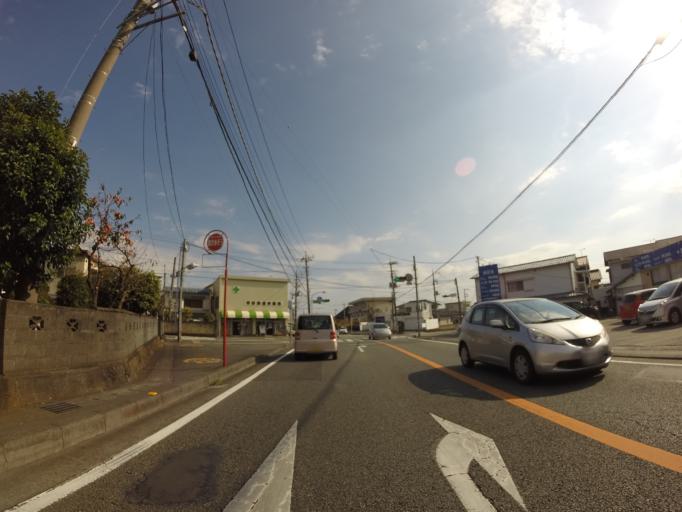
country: JP
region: Shizuoka
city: Fujinomiya
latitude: 35.2169
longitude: 138.6257
